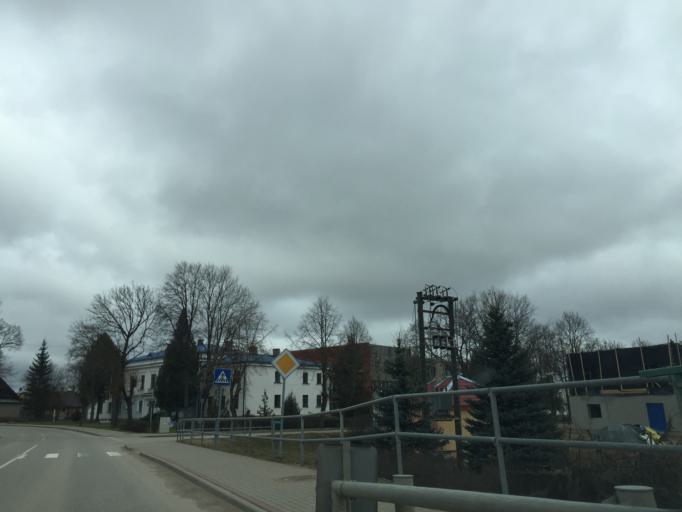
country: LV
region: Ilukste
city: Ilukste
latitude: 55.9769
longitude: 26.3009
